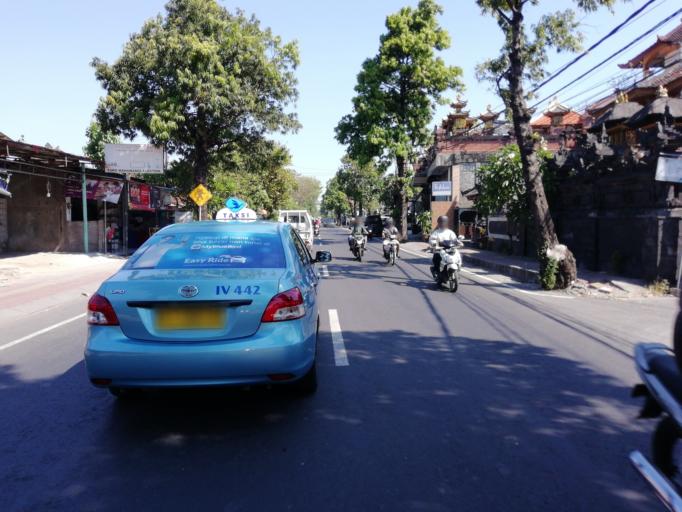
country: ID
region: Bali
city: Karyadharma
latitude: -8.7117
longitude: 115.2158
